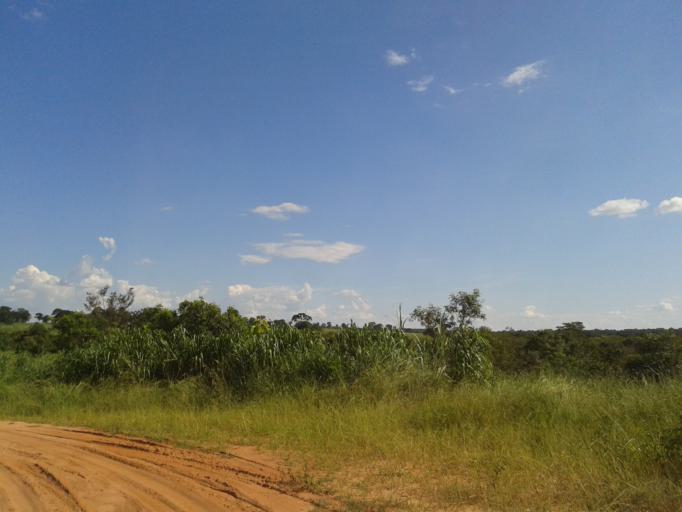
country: BR
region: Minas Gerais
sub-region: Santa Vitoria
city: Santa Vitoria
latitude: -19.1301
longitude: -50.4872
